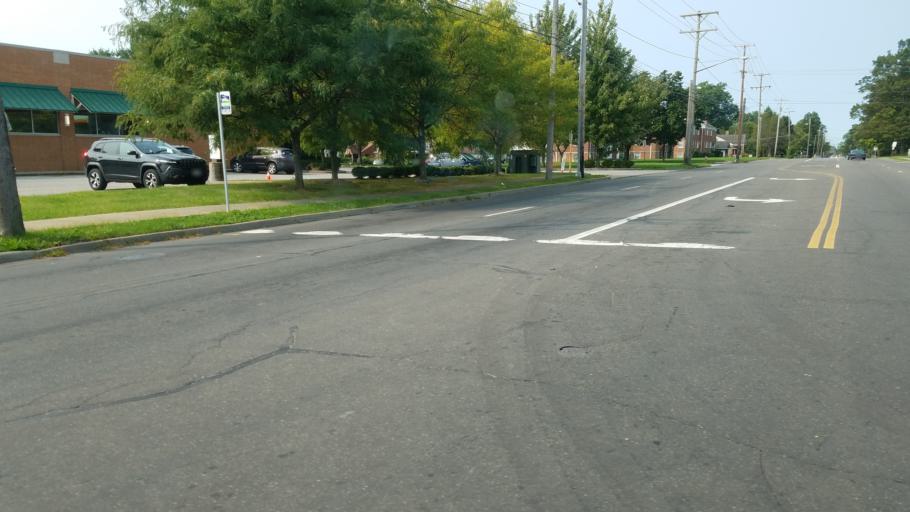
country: US
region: Ohio
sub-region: Mahoning County
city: Struthers
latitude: 41.0609
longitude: -80.6451
